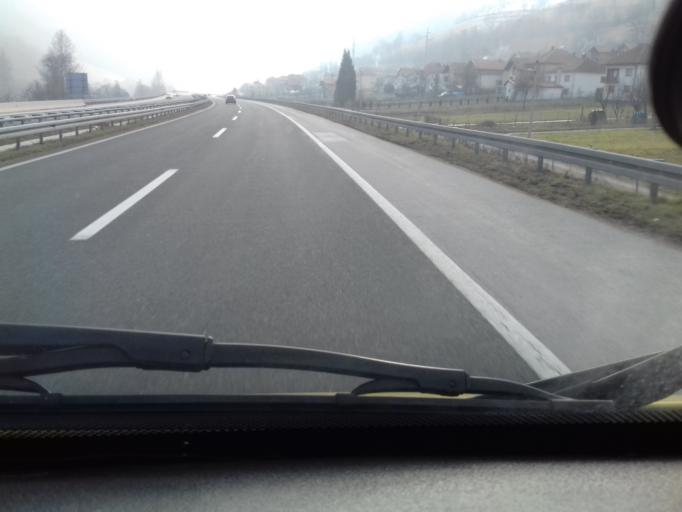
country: BA
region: Federation of Bosnia and Herzegovina
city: Dobrinje
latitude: 44.0765
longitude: 18.1082
